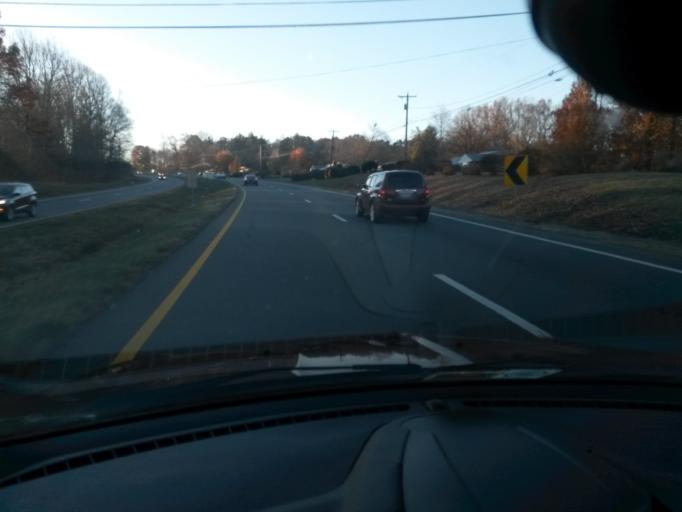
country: US
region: Virginia
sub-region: Franklin County
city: Rocky Mount
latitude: 37.0509
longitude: -79.8819
